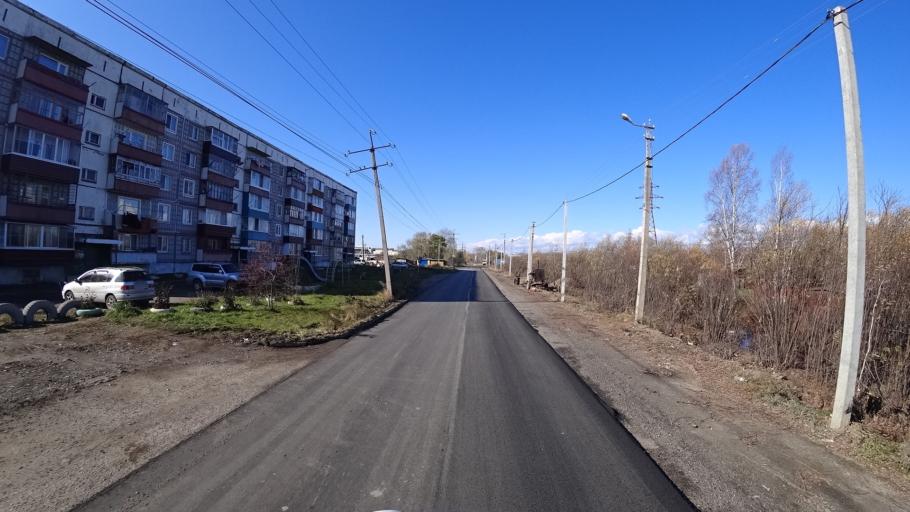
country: RU
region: Khabarovsk Krai
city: Amursk
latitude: 50.1052
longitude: 136.5163
